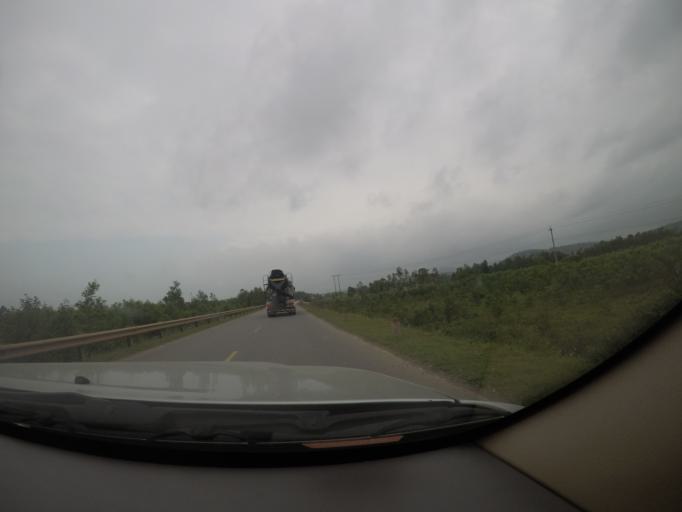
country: VN
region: Quang Binh
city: Kien Giang
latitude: 17.2494
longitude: 106.6819
